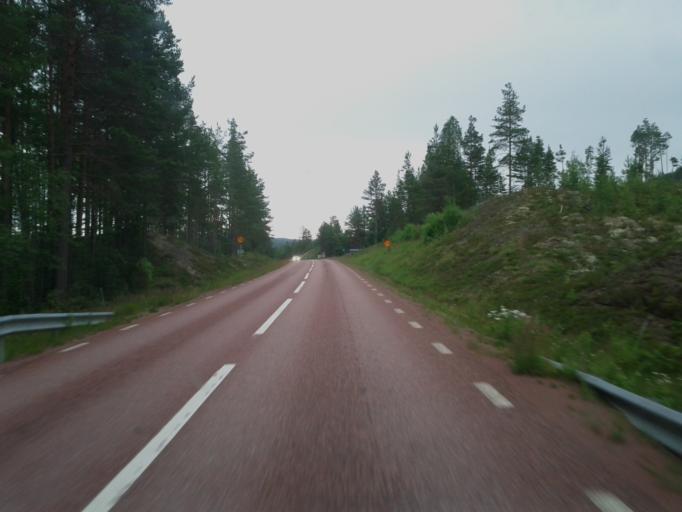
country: SE
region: Dalarna
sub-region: Alvdalens Kommun
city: AElvdalen
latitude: 61.2834
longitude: 13.7556
